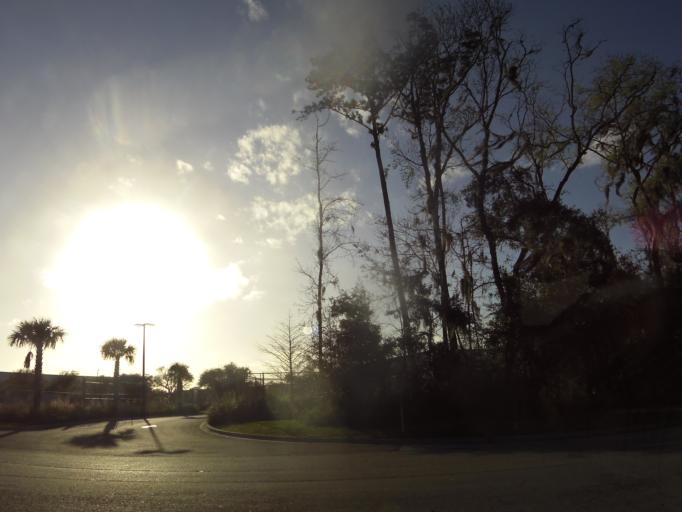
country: US
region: Florida
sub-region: Duval County
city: Jacksonville
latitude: 30.2638
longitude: -81.6033
